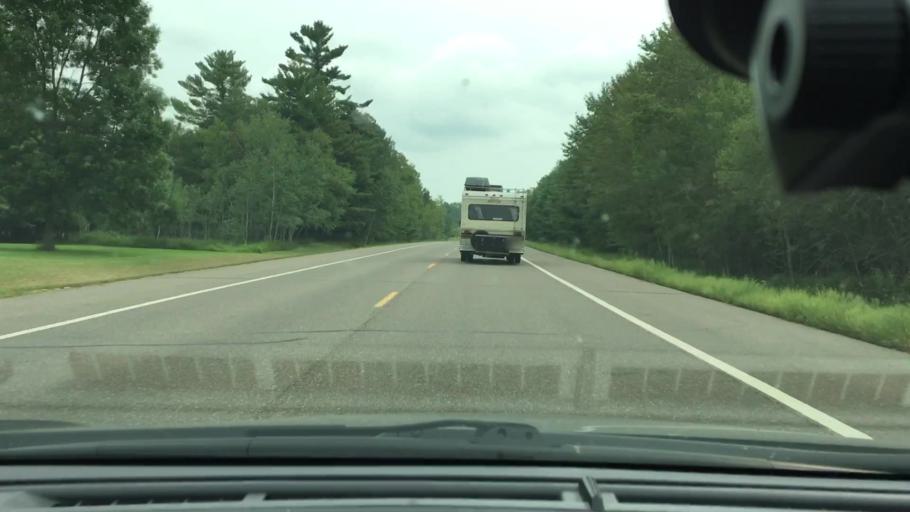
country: US
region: Minnesota
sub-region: Crow Wing County
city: Crosby
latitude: 46.4105
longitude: -93.8525
